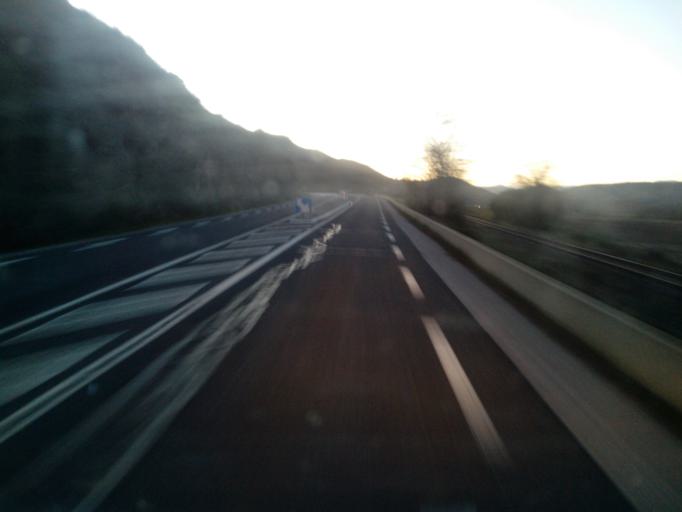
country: FR
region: Languedoc-Roussillon
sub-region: Departement des Pyrenees-Orientales
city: Estagel
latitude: 42.7718
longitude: 2.7547
